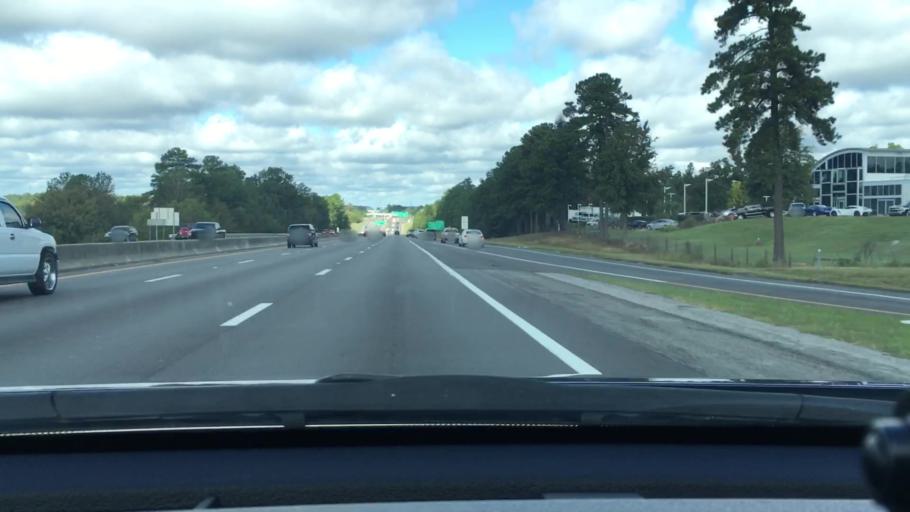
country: US
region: South Carolina
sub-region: Lexington County
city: Irmo
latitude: 34.0801
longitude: -81.1547
